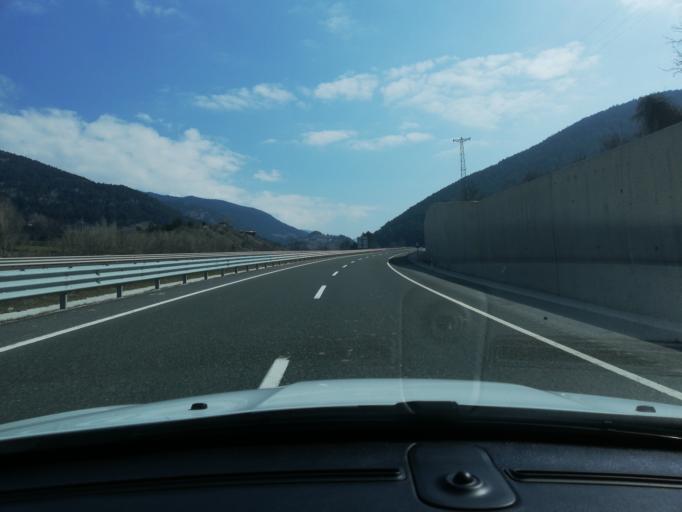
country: TR
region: Cankiri
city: Ilgaz
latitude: 41.0278
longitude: 33.7273
